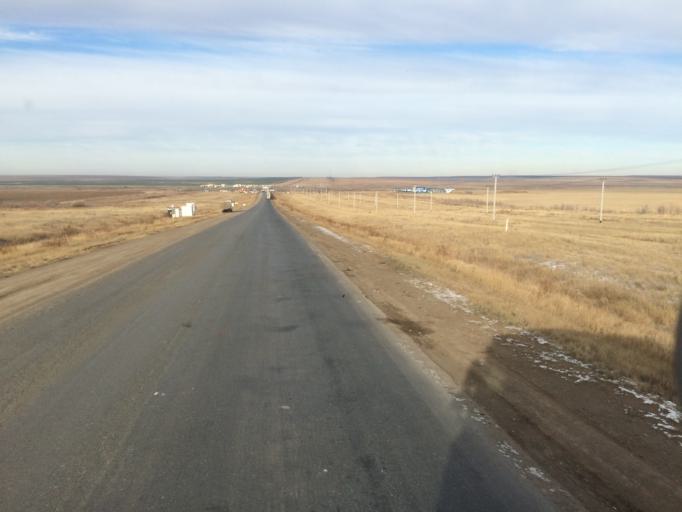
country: KZ
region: Batys Qazaqstan
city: Peremetnoe
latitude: 51.6560
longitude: 51.0095
